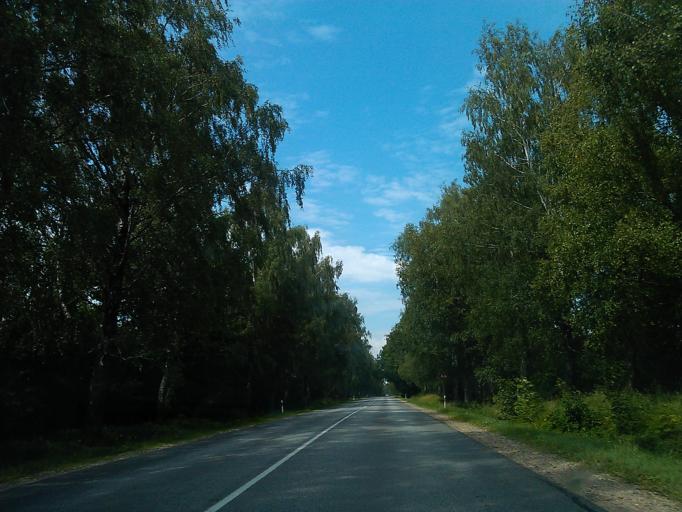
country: LV
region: Burtnieki
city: Matisi
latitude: 57.6891
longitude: 25.1758
